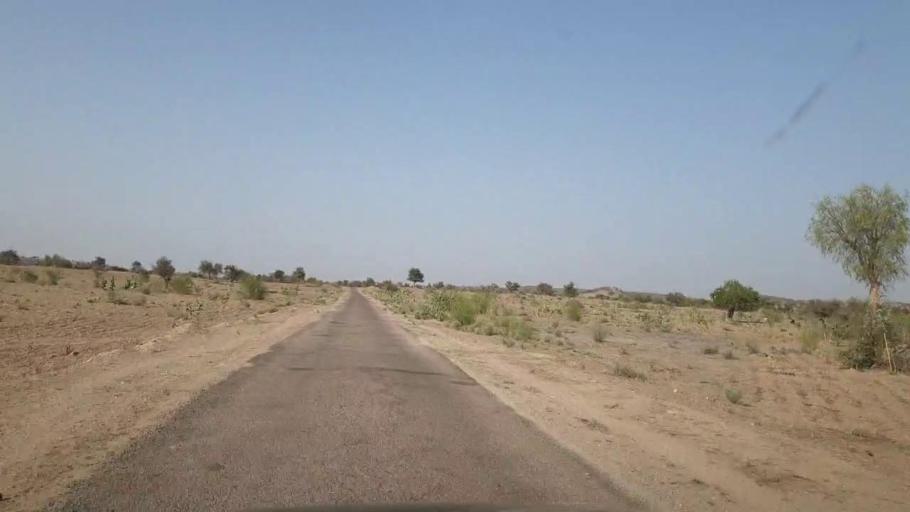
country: PK
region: Sindh
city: Islamkot
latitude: 25.1290
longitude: 70.5161
